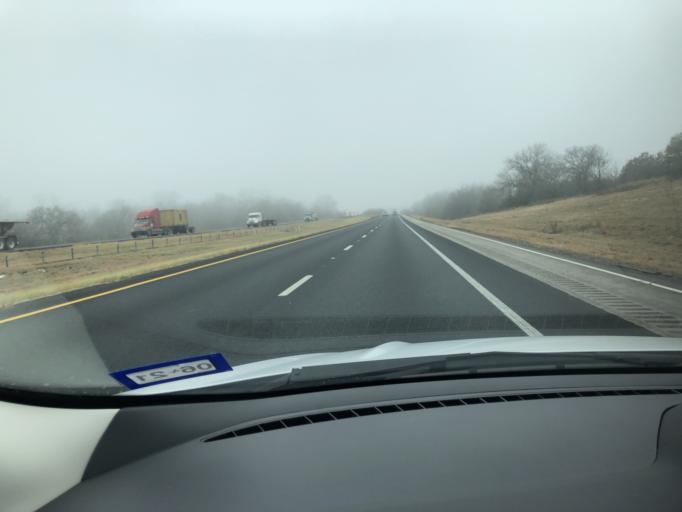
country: US
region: Texas
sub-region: Gonzales County
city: Waelder
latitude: 29.6632
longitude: -97.3767
